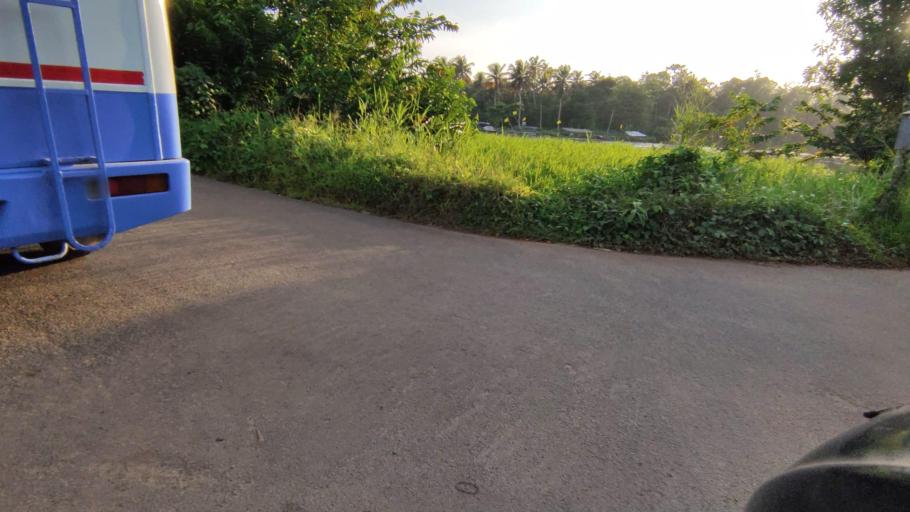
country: IN
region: Kerala
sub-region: Kottayam
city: Kottayam
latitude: 9.5768
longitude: 76.4468
